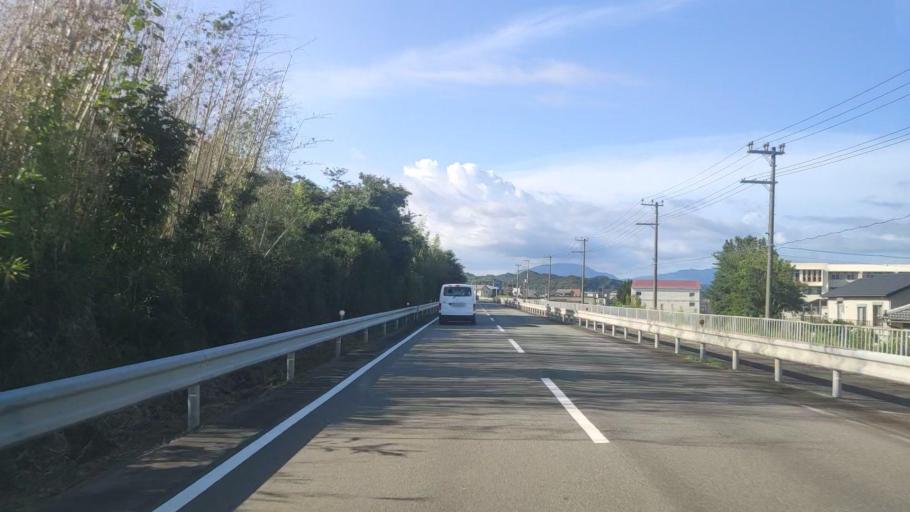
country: JP
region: Wakayama
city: Tanabe
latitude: 33.6728
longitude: 135.4079
